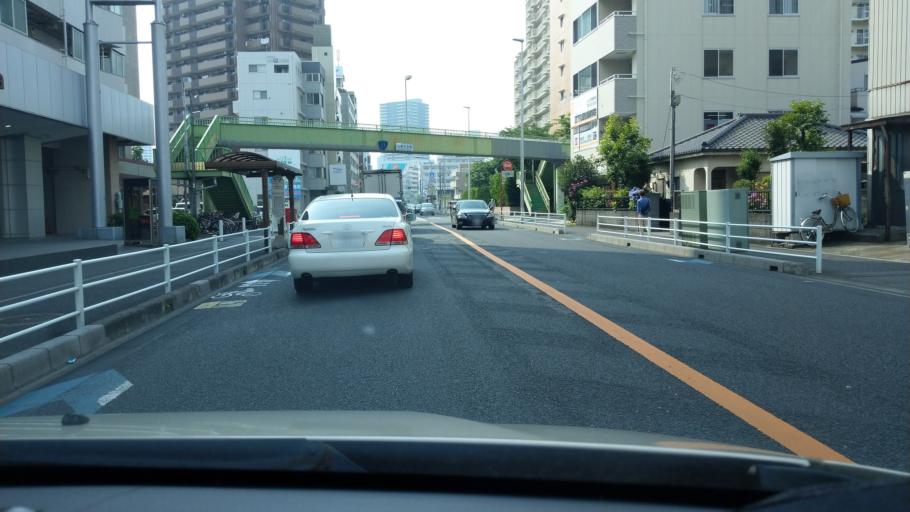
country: JP
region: Saitama
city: Shimotoda
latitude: 35.8430
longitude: 139.6549
